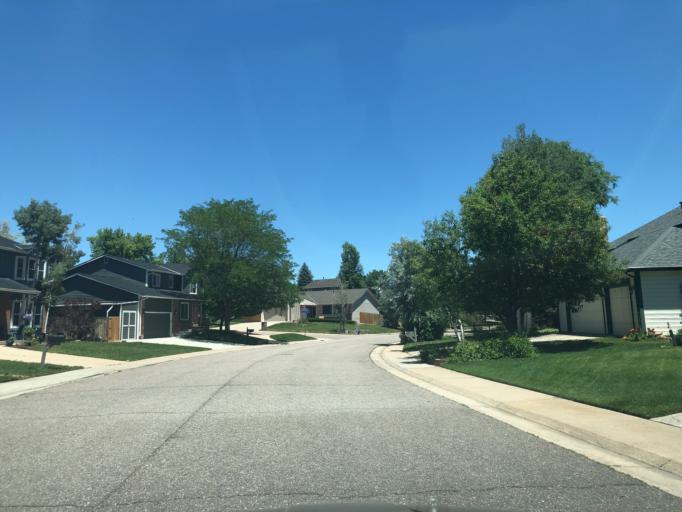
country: US
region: Colorado
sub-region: Arapahoe County
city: Dove Valley
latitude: 39.6156
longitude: -104.7761
